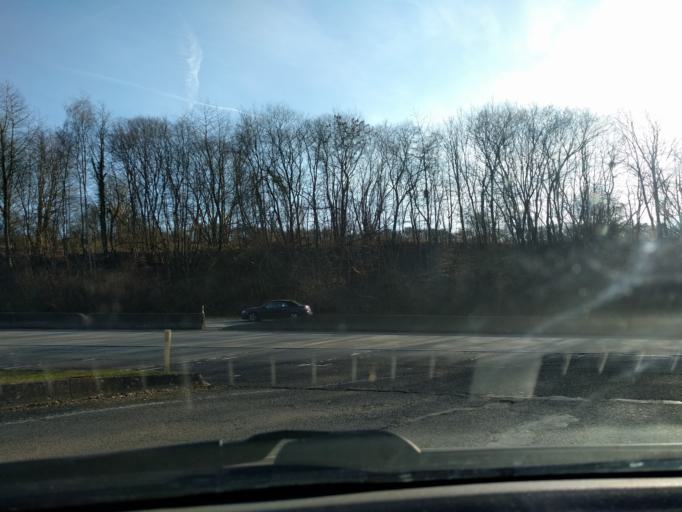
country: BE
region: Wallonia
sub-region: Province de Namur
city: Dinant
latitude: 50.2389
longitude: 4.9294
